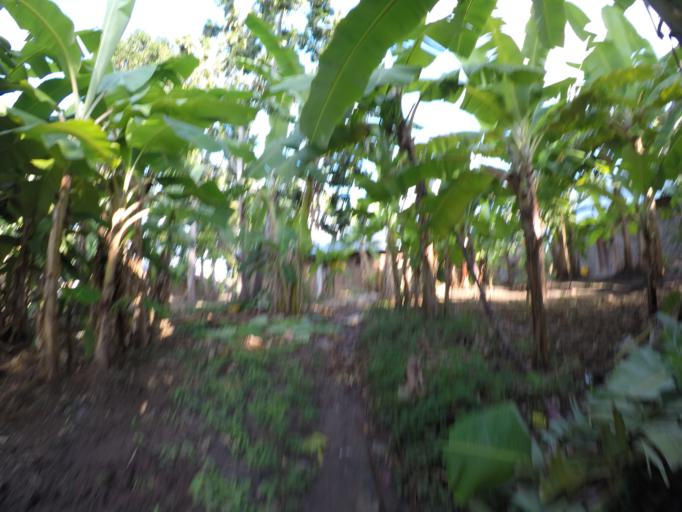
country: TZ
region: Pemba South
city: Mtambile
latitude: -5.3886
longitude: 39.7460
